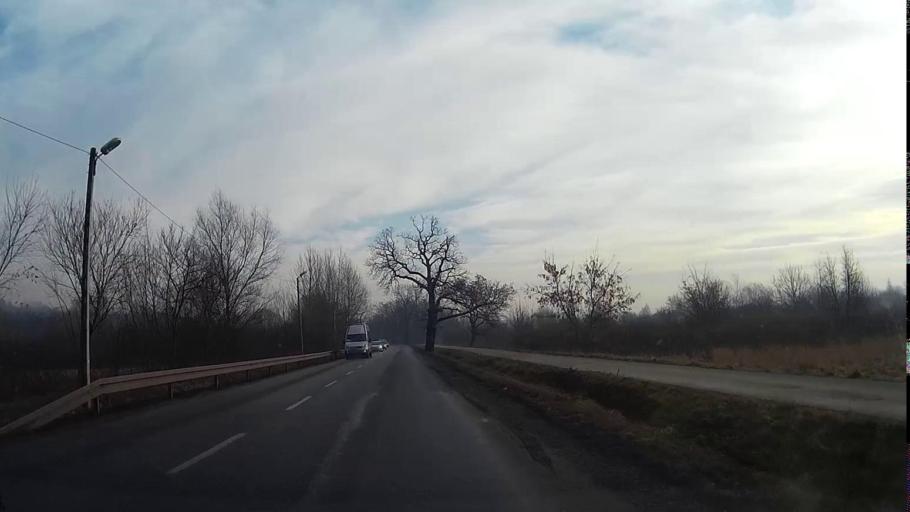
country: PL
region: Lesser Poland Voivodeship
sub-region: Krakow
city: Sidzina
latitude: 50.0461
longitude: 19.8785
